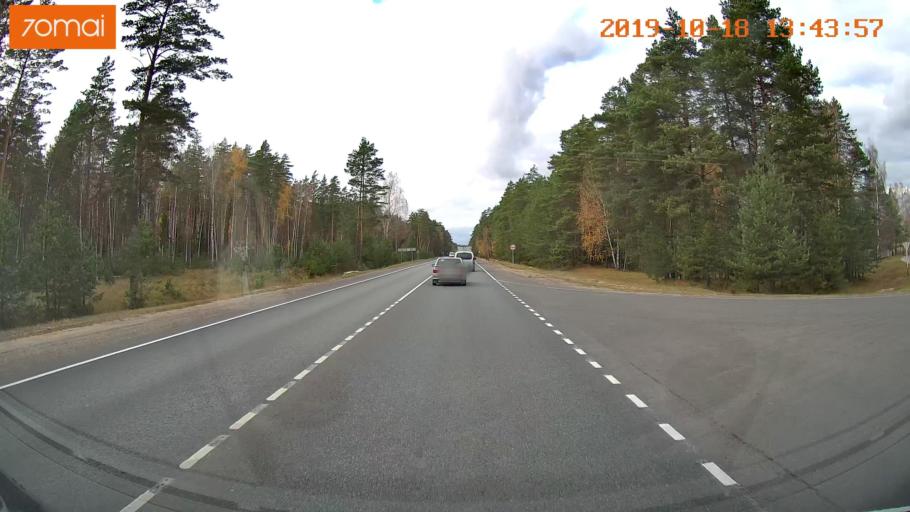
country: RU
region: Rjazan
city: Solotcha
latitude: 54.9337
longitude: 39.9699
